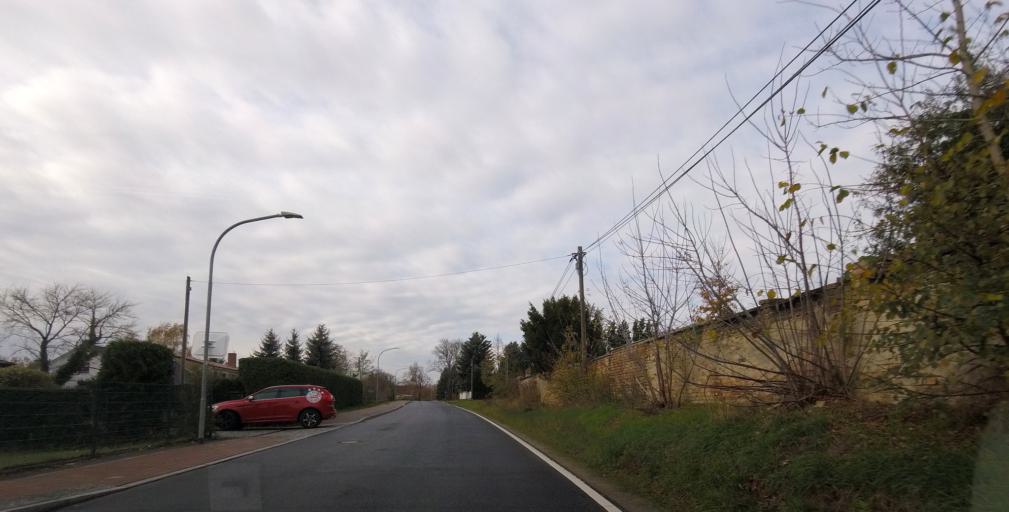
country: DE
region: Brandenburg
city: Treuenbrietzen
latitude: 52.0945
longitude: 12.8565
